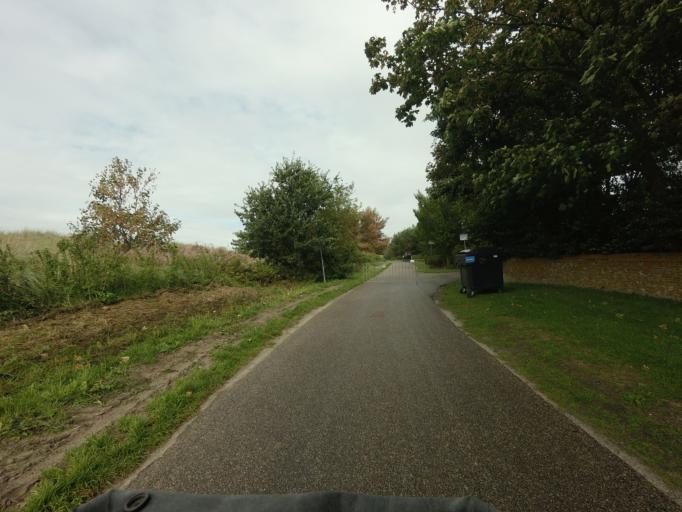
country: NL
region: Friesland
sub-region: Gemeente Ameland
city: Nes
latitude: 53.4484
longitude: 5.7815
